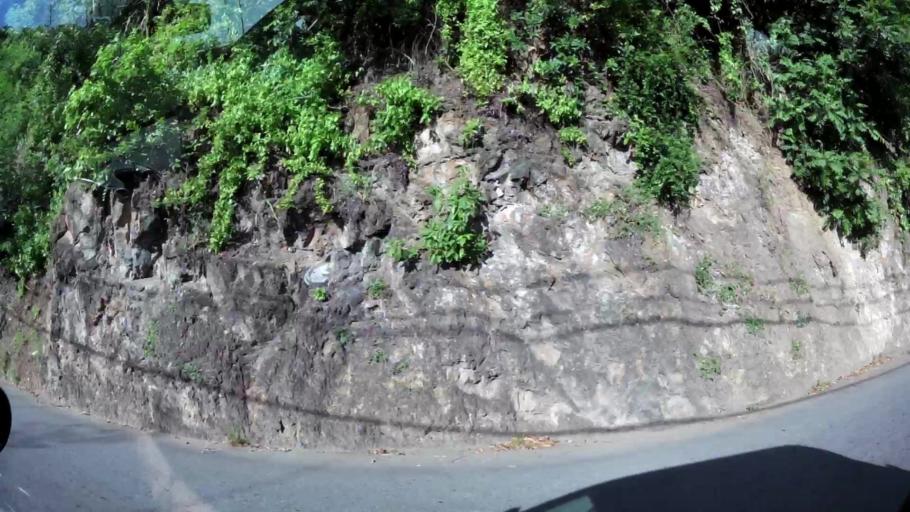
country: TT
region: Eastern Tobago
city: Roxborough
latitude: 11.2319
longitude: -60.6057
